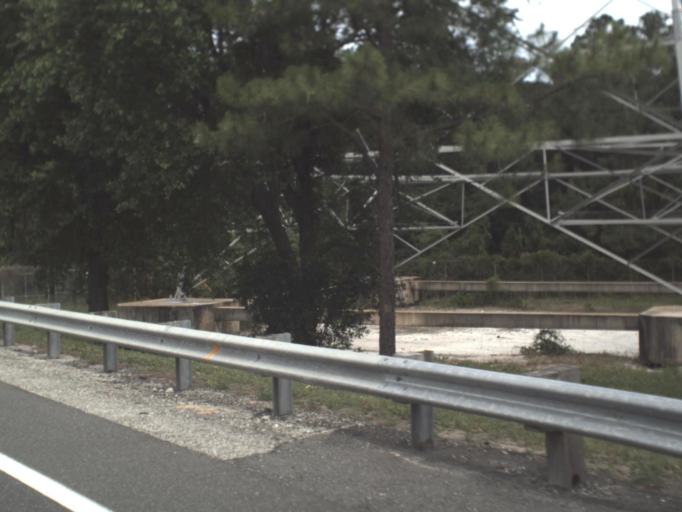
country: US
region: Florida
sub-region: Duval County
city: Jacksonville
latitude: 30.4145
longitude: -81.5441
